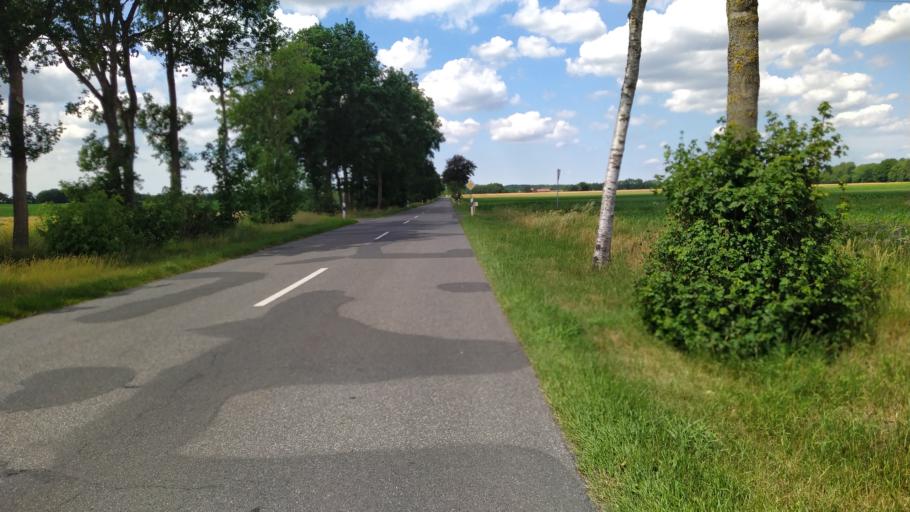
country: DE
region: Lower Saxony
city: Hollnseth
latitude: 53.5760
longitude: 9.1123
